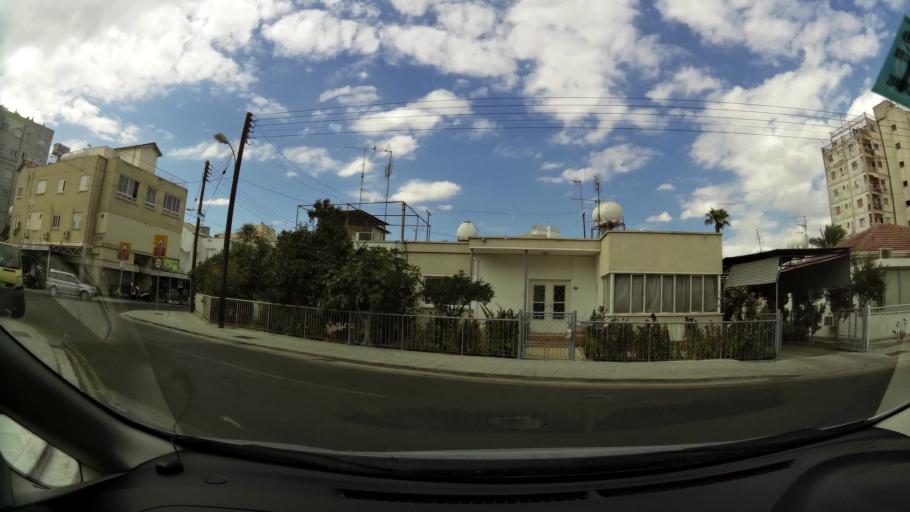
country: CY
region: Lefkosia
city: Nicosia
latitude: 35.1798
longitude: 33.3848
